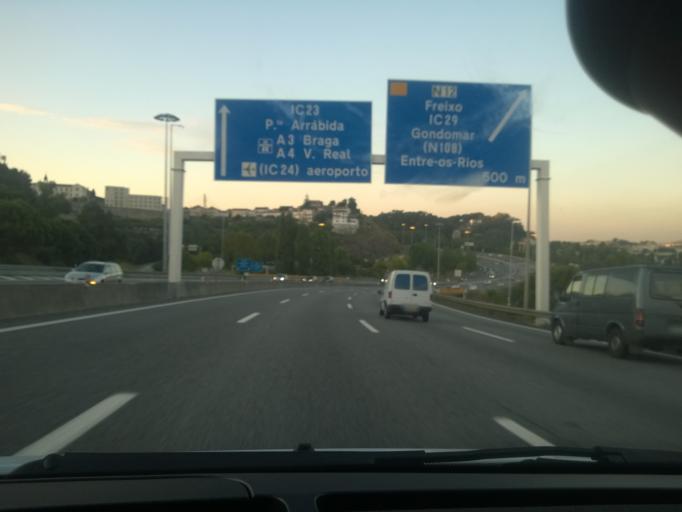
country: PT
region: Porto
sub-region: Gondomar
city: Valbom
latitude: 41.1459
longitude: -8.5810
